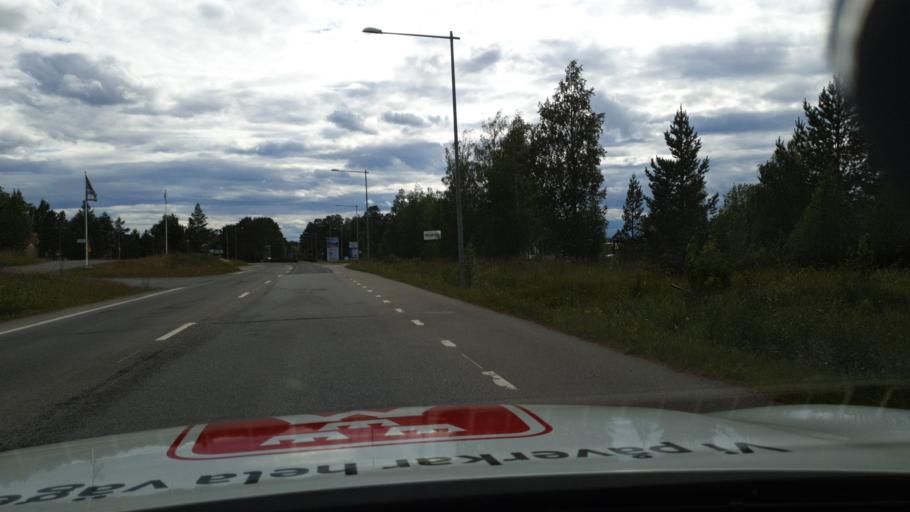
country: SE
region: Jaemtland
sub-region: OEstersunds Kommun
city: Ostersund
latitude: 63.1899
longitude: 14.6542
